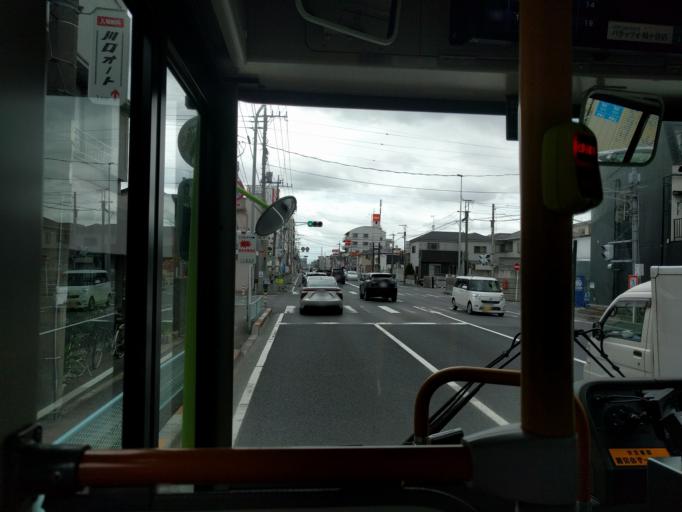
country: JP
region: Saitama
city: Kawaguchi
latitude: 35.8085
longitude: 139.7340
